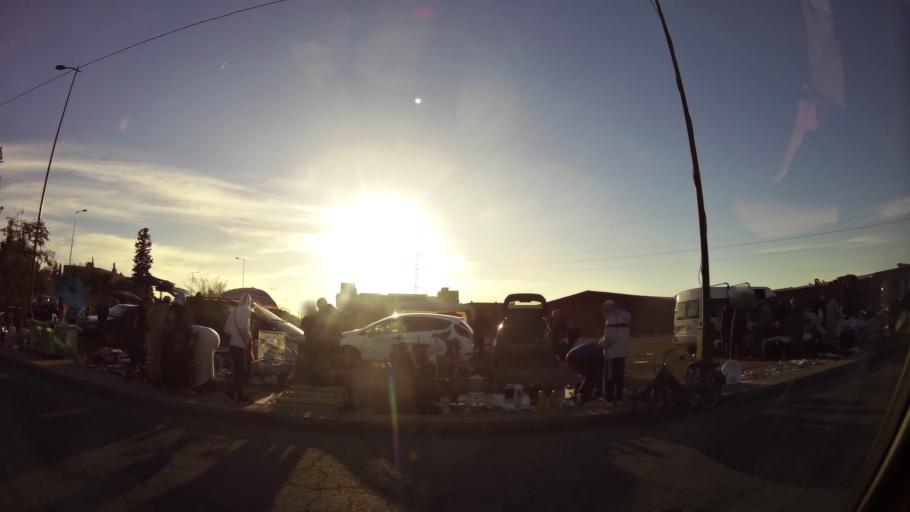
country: MA
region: Marrakech-Tensift-Al Haouz
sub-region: Marrakech
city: Marrakesh
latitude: 31.6226
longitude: -8.0437
